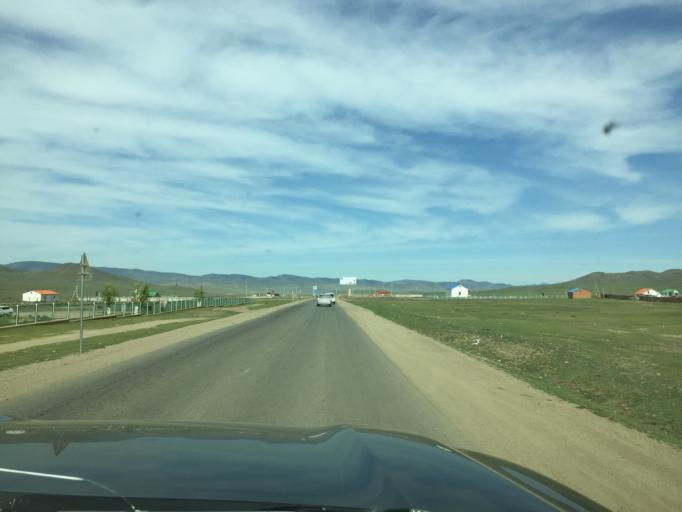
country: MN
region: Central Aimak
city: Ihsueuej
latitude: 48.2268
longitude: 106.2891
